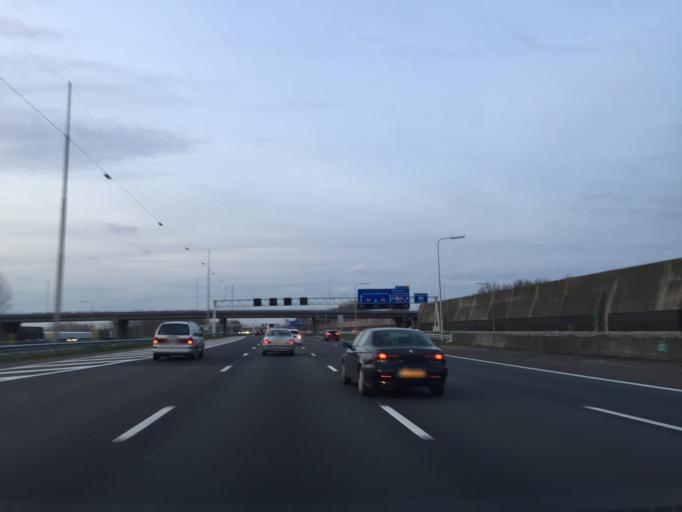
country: NL
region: South Holland
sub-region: Gemeente Ridderkerk
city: Ridderkerk
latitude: 51.8628
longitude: 4.5902
